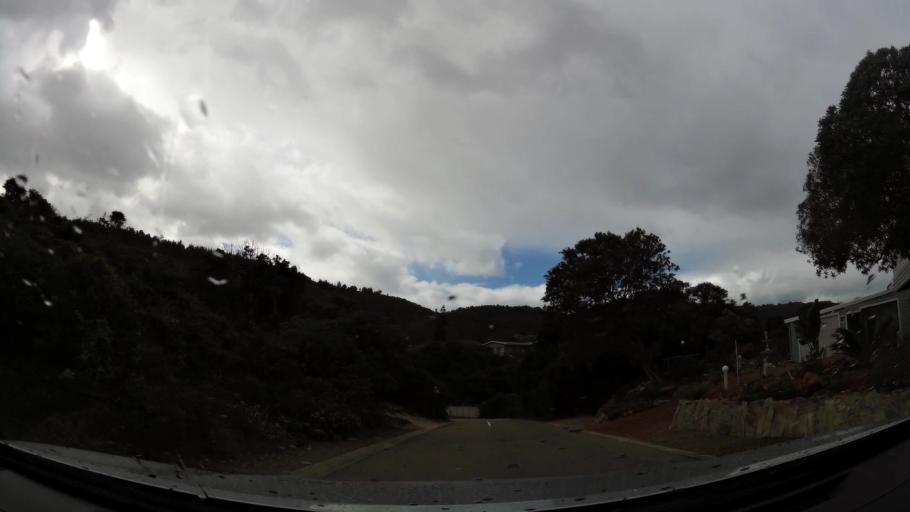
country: ZA
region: Western Cape
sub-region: Eden District Municipality
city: George
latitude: -34.0497
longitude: 22.3104
